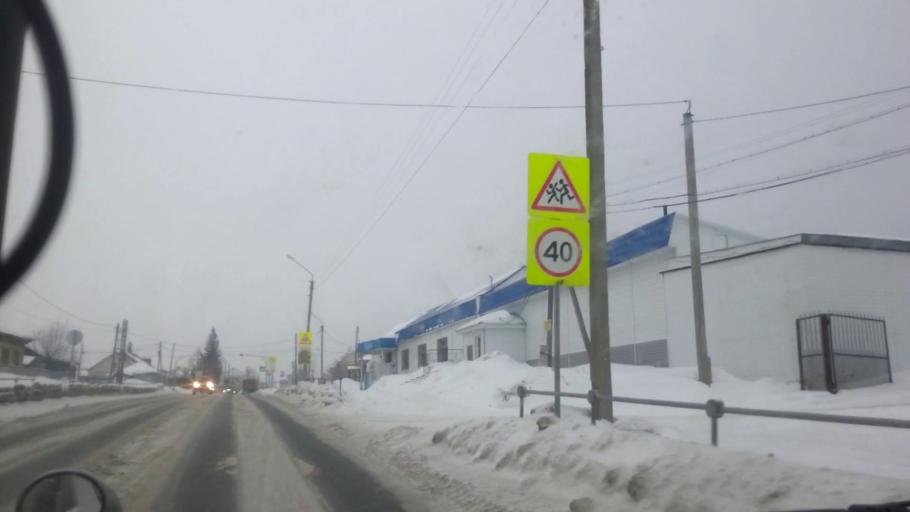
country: RU
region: Altai Krai
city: Vlasikha
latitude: 53.2960
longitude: 83.5813
